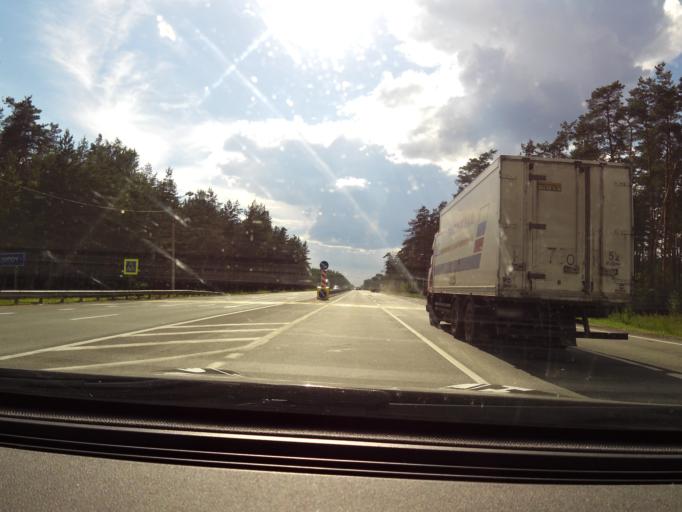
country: RU
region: Nizjnij Novgorod
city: Pyra
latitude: 56.2948
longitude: 43.3896
